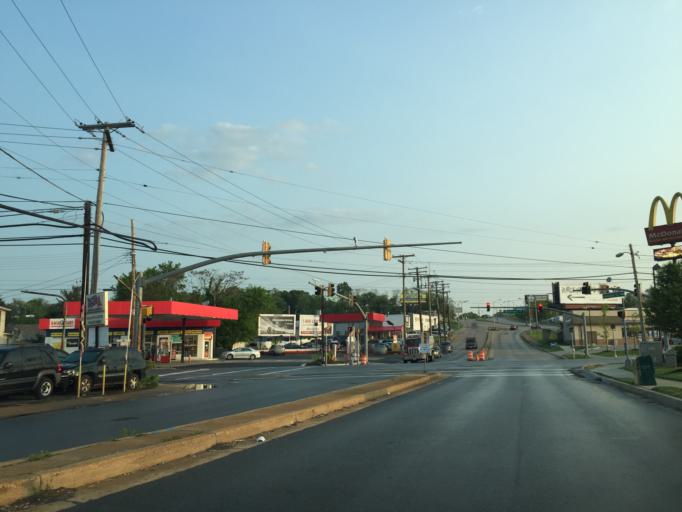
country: US
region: Maryland
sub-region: Baltimore County
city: Lansdowne
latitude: 39.2567
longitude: -76.6643
